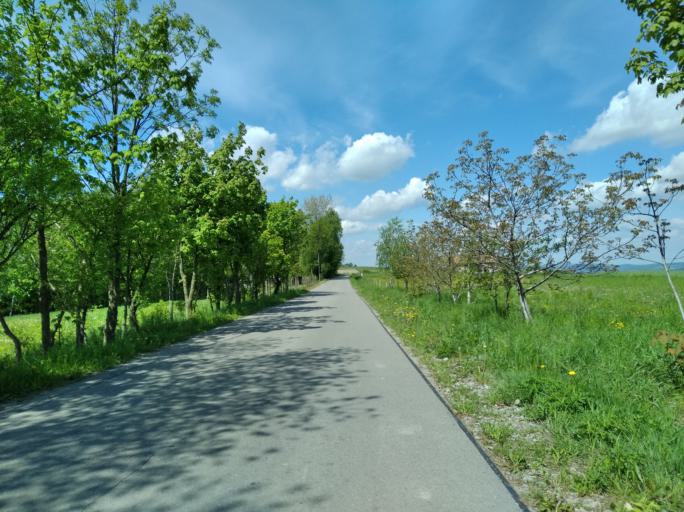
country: PL
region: Subcarpathian Voivodeship
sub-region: Powiat jasielski
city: Kolaczyce
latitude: 49.8393
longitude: 21.4964
